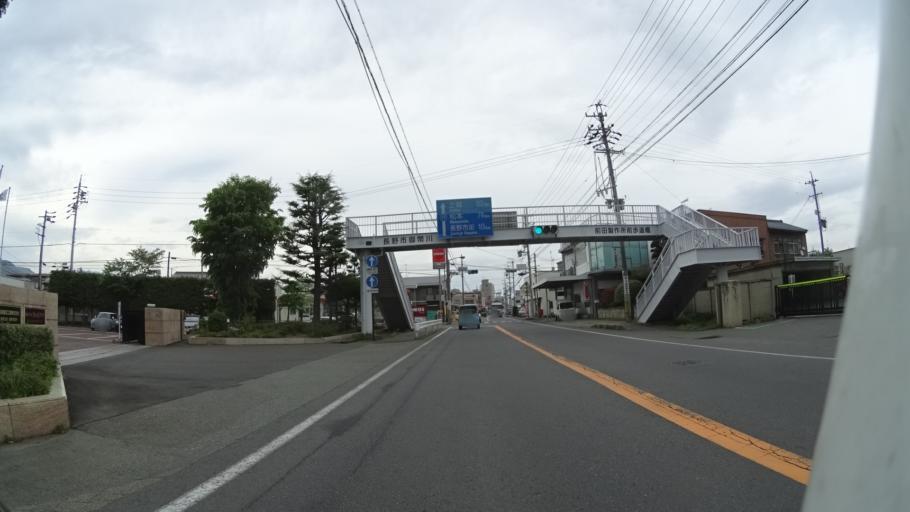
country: JP
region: Nagano
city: Nagano-shi
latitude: 36.5722
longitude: 138.1424
